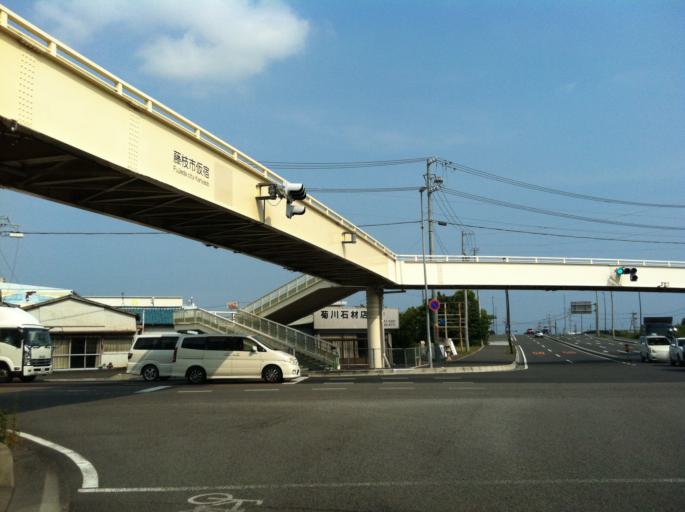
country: JP
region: Shizuoka
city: Fujieda
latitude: 34.8940
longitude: 138.2820
